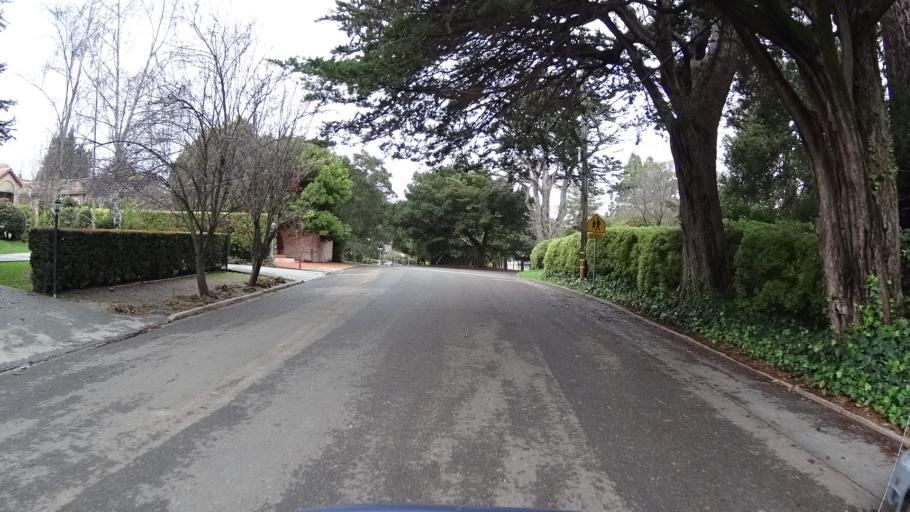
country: US
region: California
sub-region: San Mateo County
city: San Mateo
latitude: 37.5678
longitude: -122.3419
